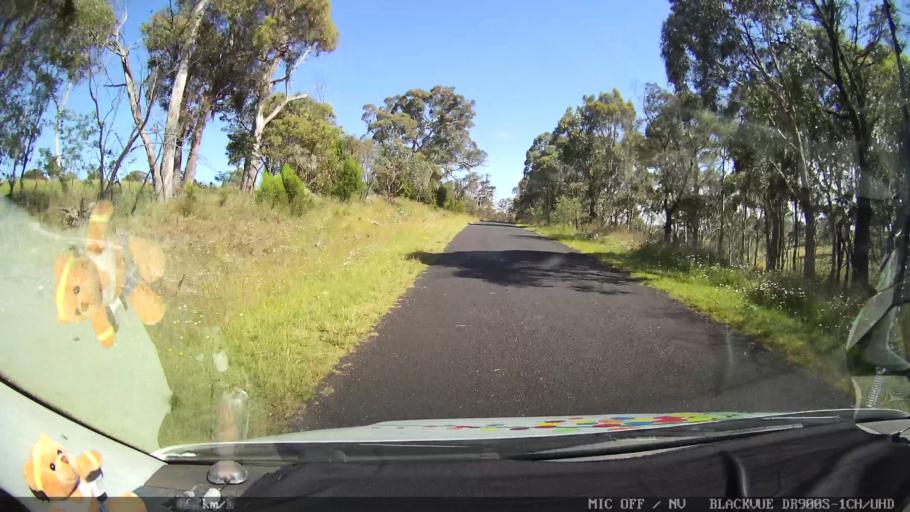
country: AU
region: New South Wales
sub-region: Guyra
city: Guyra
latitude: -30.0631
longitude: 151.6655
